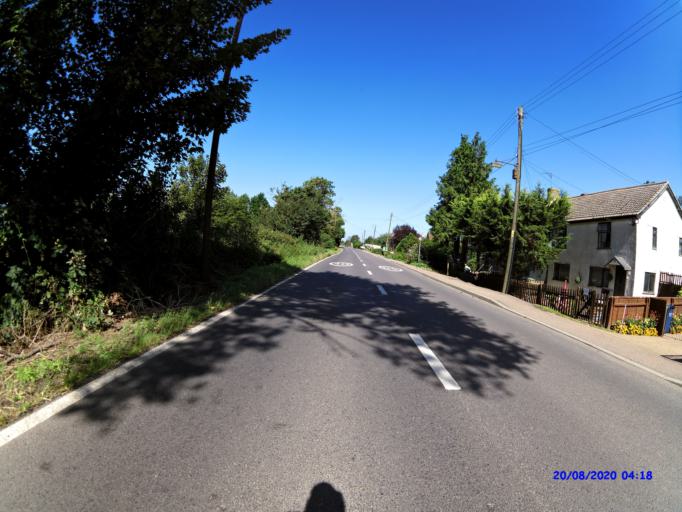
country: GB
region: England
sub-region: Cambridgeshire
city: Ramsey
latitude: 52.4906
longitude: -0.1163
